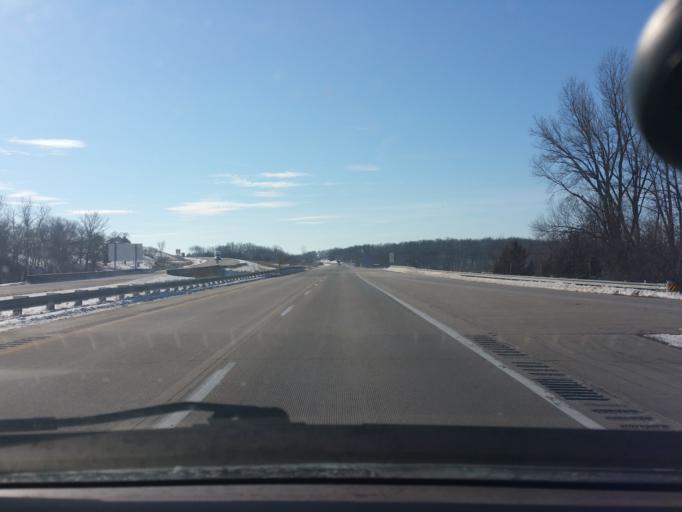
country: US
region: Iowa
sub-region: Clarke County
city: Osceola
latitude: 41.0100
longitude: -93.7972
